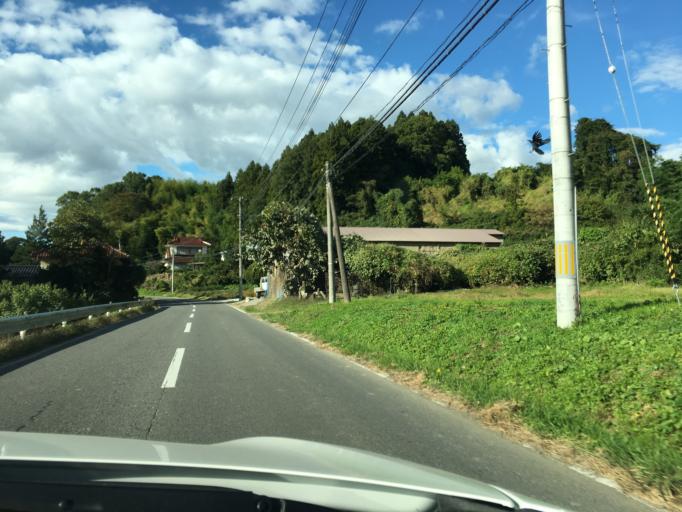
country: JP
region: Fukushima
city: Sukagawa
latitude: 37.2475
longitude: 140.4421
